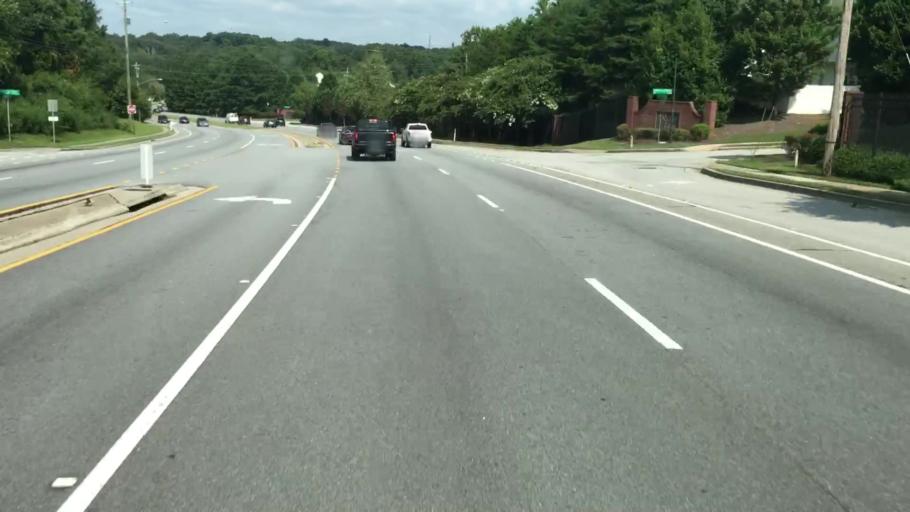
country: US
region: Georgia
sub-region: Gwinnett County
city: Lawrenceville
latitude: 33.9413
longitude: -84.0368
